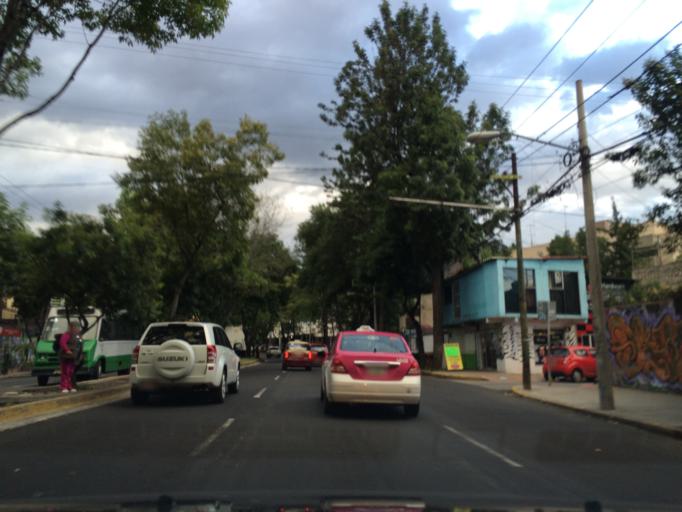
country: MX
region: Mexico City
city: Colonia del Valle
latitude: 19.3696
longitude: -99.1622
